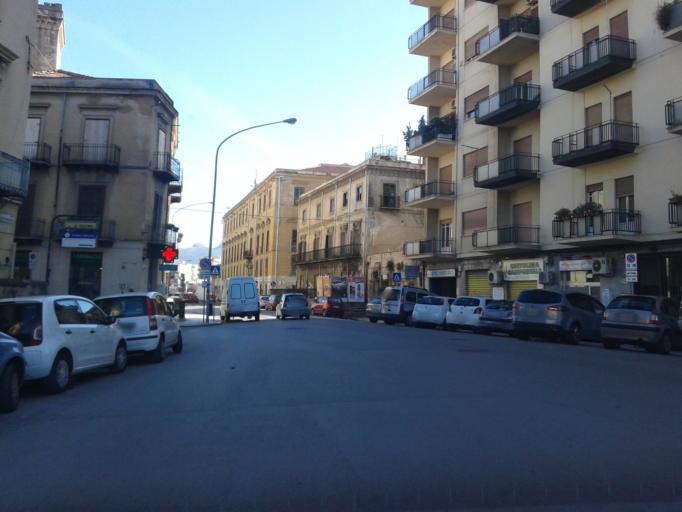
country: IT
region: Sicily
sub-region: Palermo
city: Palermo
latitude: 38.1192
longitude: 13.3418
